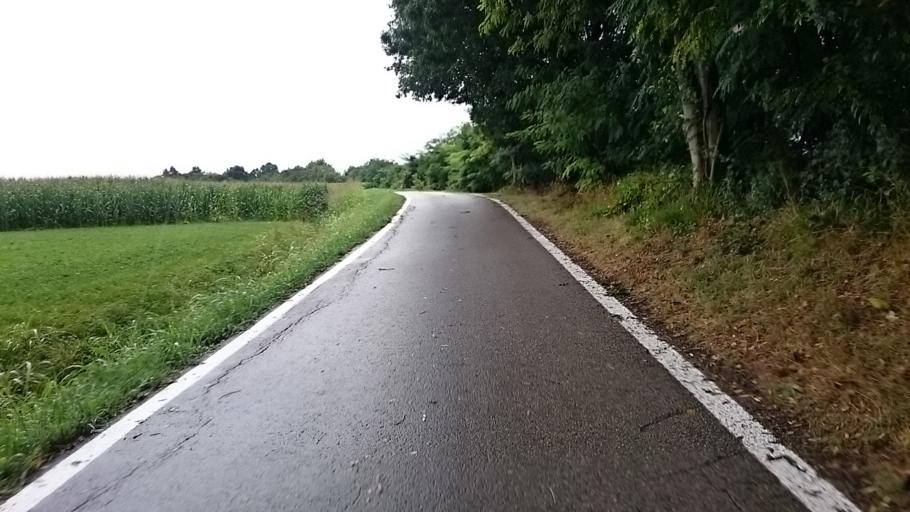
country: IT
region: Veneto
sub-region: Provincia di Treviso
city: Villa d'Asolo
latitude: 45.7589
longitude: 11.8804
